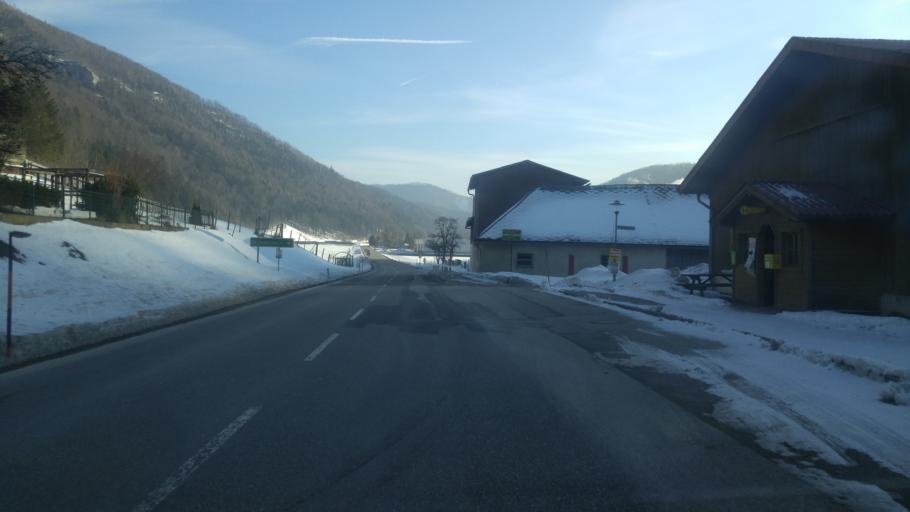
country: AT
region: Lower Austria
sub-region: Politischer Bezirk Lilienfeld
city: Hohenberg
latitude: 47.9345
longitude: 15.6023
